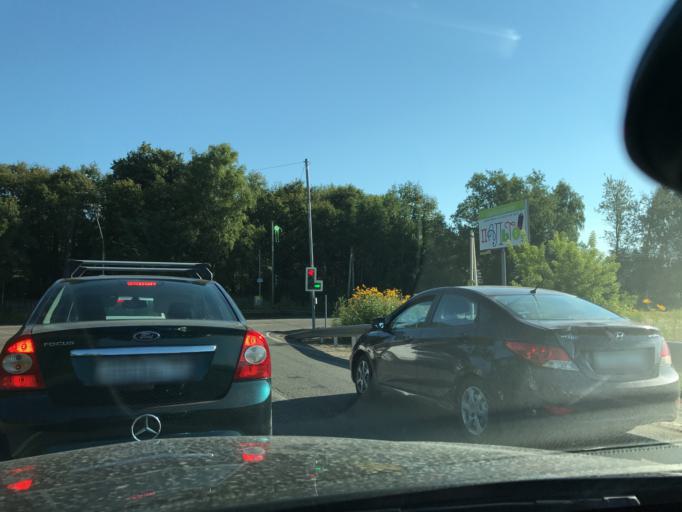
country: RU
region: Moskovskaya
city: Sverdlovskiy
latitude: 55.8868
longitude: 38.1645
